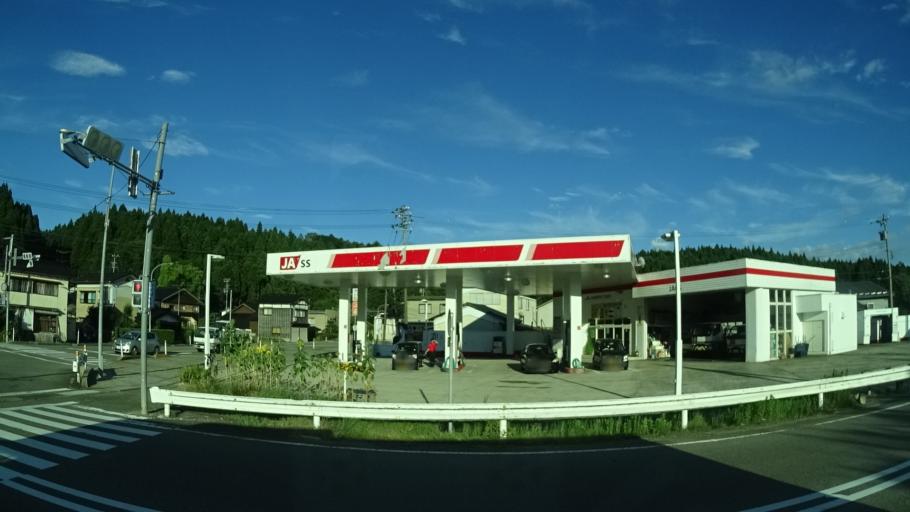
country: JP
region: Ishikawa
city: Nanao
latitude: 37.2437
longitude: 136.8991
